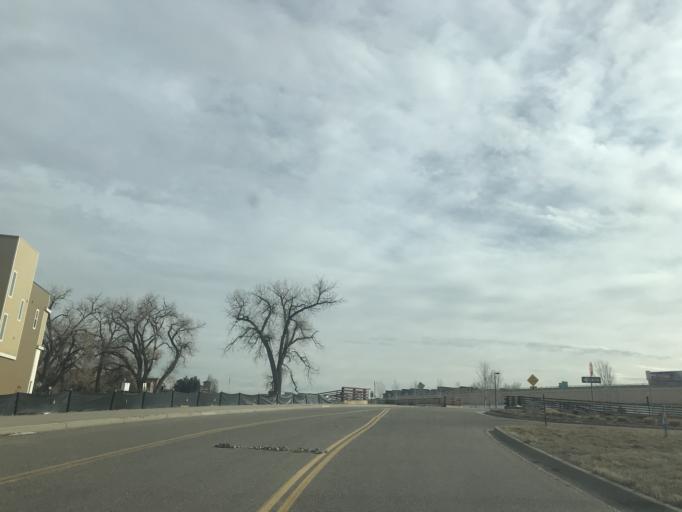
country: US
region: Colorado
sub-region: Arapahoe County
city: Columbine Valley
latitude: 39.5651
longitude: -105.0211
